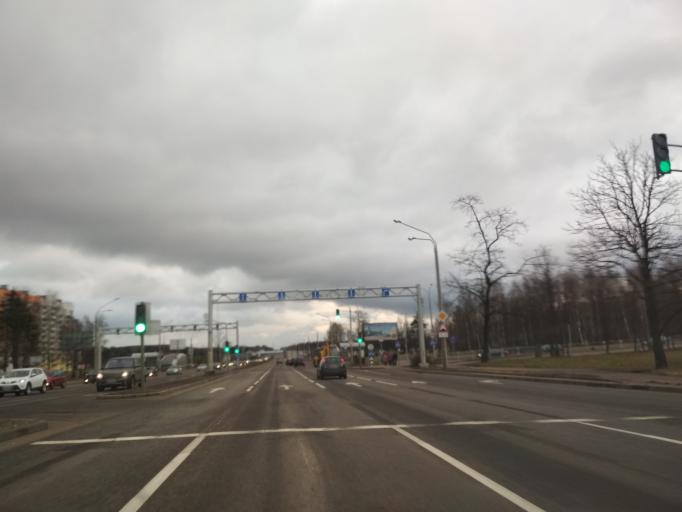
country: BY
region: Minsk
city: Vyaliki Trastsyanets
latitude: 53.8498
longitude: 27.7020
